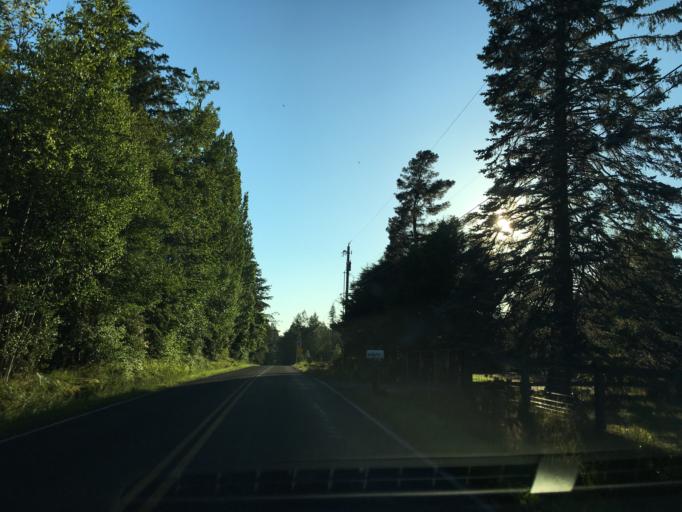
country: US
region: Washington
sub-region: Whatcom County
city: Geneva
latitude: 48.8186
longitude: -122.3896
